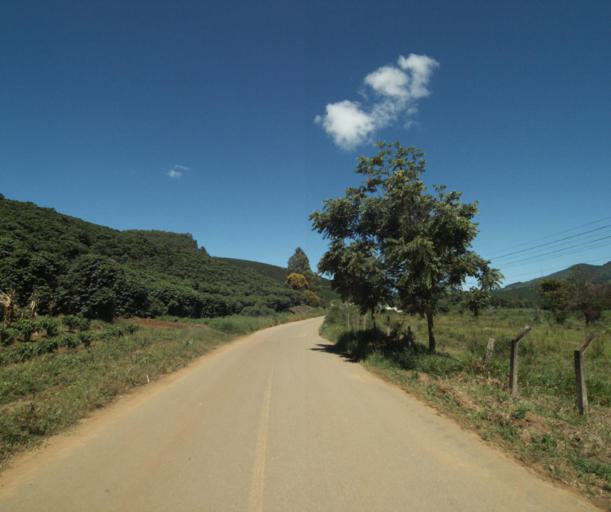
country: BR
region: Minas Gerais
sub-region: Espera Feliz
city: Espera Feliz
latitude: -20.5604
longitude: -41.8228
